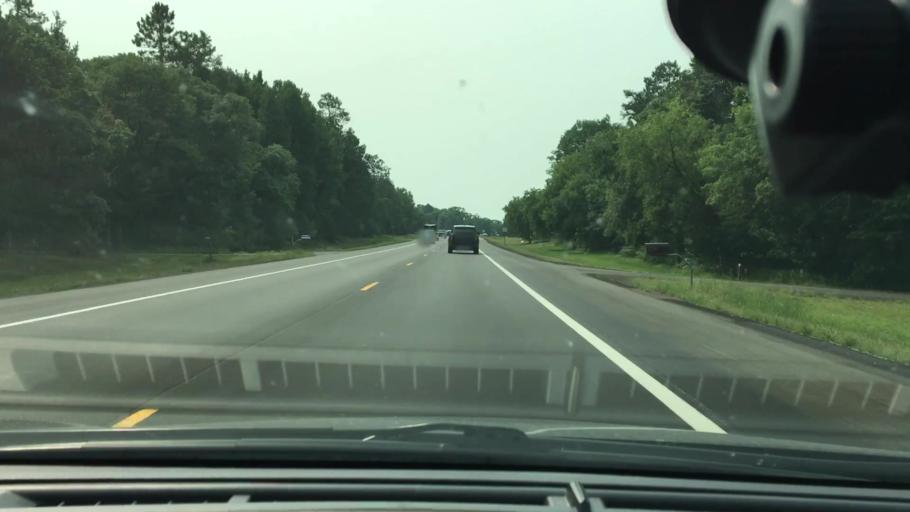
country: US
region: Minnesota
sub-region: Crow Wing County
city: Brainerd
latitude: 46.4408
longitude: -94.1716
